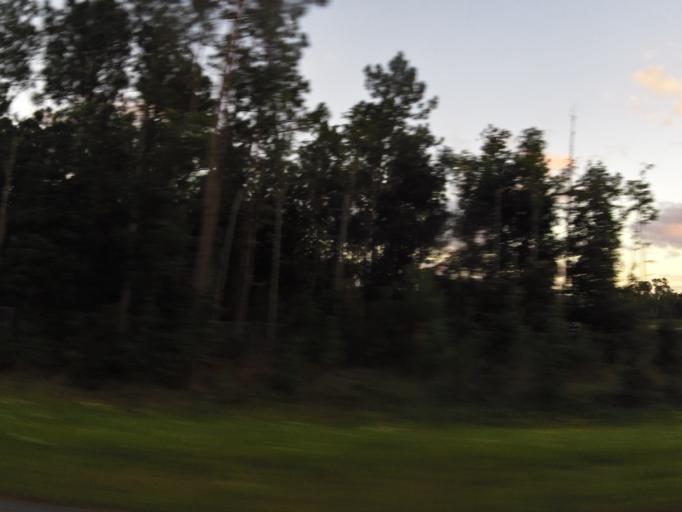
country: US
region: Florida
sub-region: Saint Johns County
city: Palm Valley
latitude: 30.0925
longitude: -81.4608
